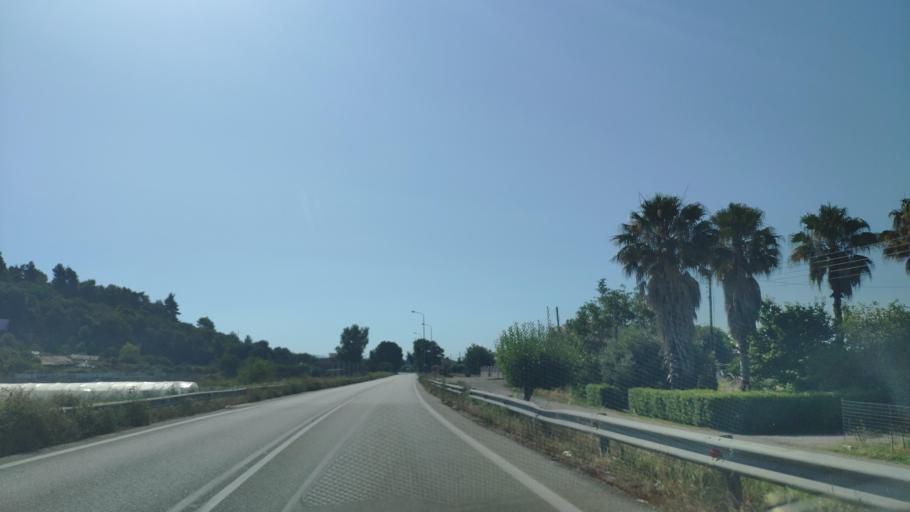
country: GR
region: West Greece
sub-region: Nomos Aitolias kai Akarnanias
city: Lepenou
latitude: 38.6848
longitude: 21.2590
